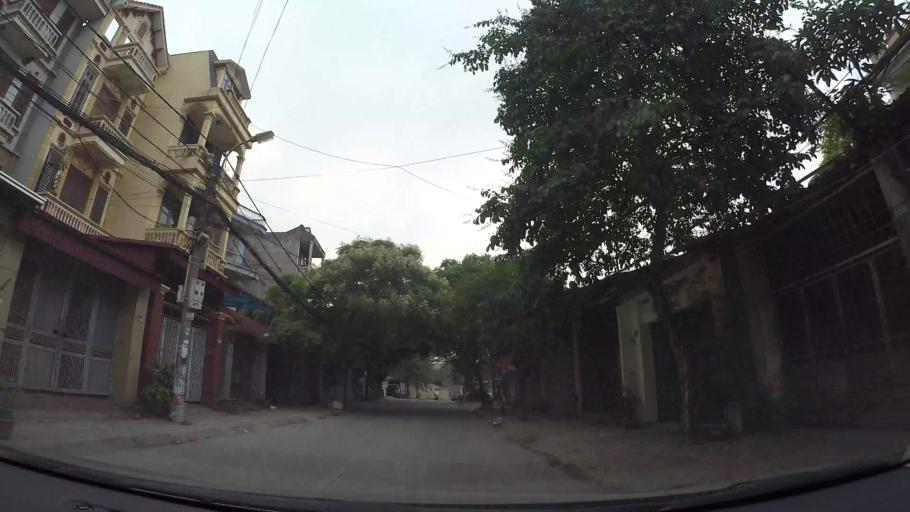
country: VN
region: Ha Noi
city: Hoan Kiem
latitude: 21.0677
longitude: 105.8834
